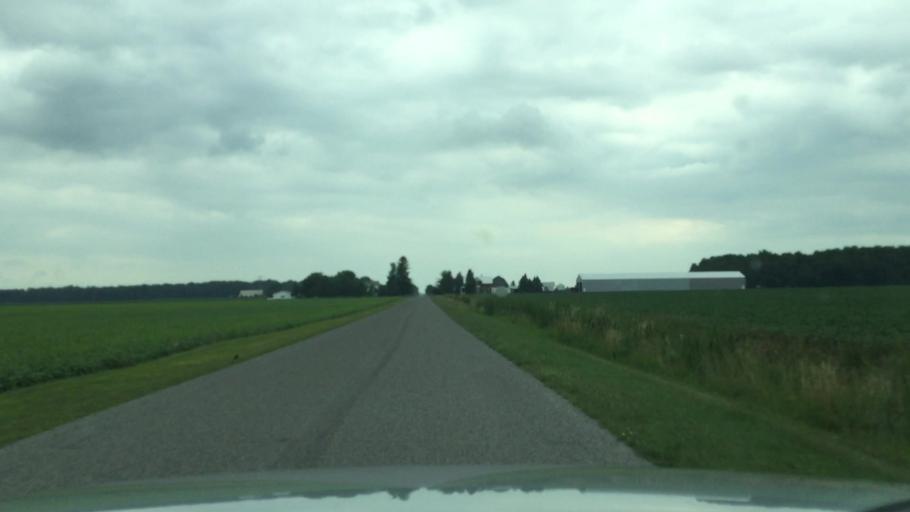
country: US
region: Michigan
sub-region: Saginaw County
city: Frankenmuth
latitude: 43.3392
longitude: -83.7786
